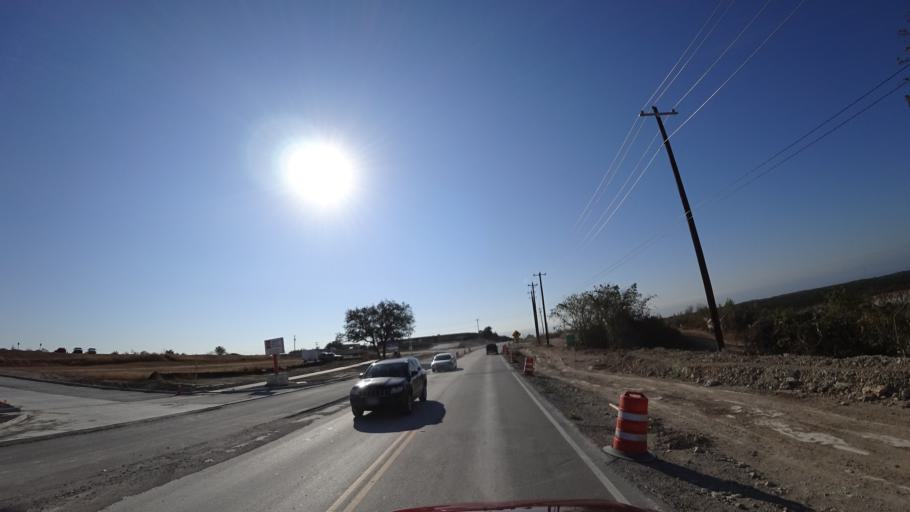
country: US
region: Texas
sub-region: Williamson County
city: Cedar Park
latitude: 30.5086
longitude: -97.8570
